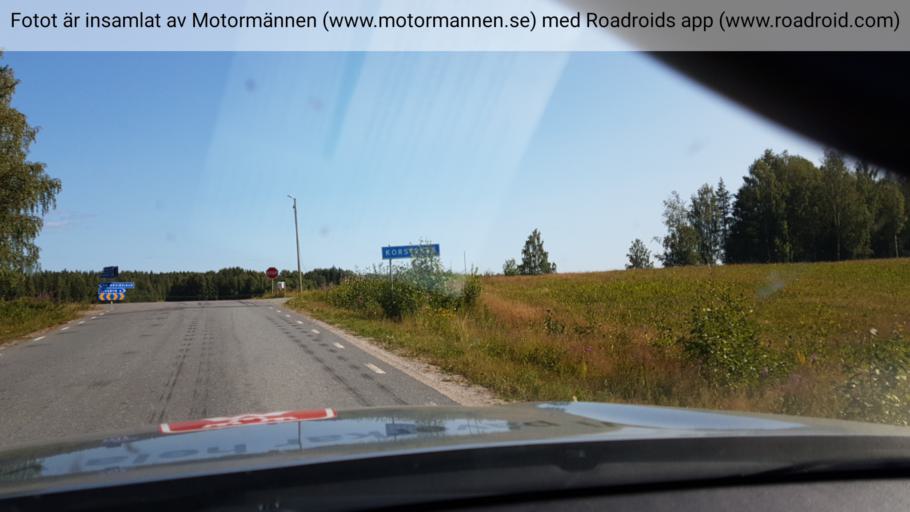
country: SE
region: Norrbotten
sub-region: Alvsbyns Kommun
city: AElvsbyn
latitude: 65.6662
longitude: 20.8905
